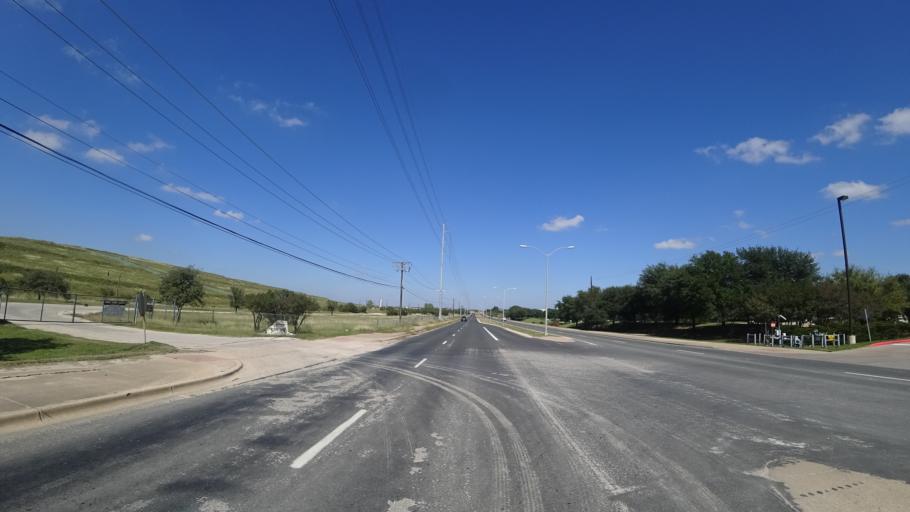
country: US
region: Texas
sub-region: Travis County
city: Manor
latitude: 30.3363
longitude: -97.6204
